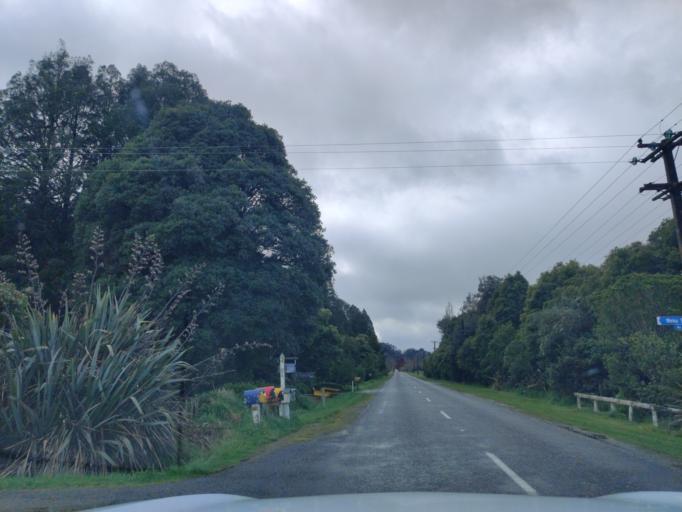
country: NZ
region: Manawatu-Wanganui
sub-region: Palmerston North City
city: Palmerston North
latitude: -40.1766
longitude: 175.7909
